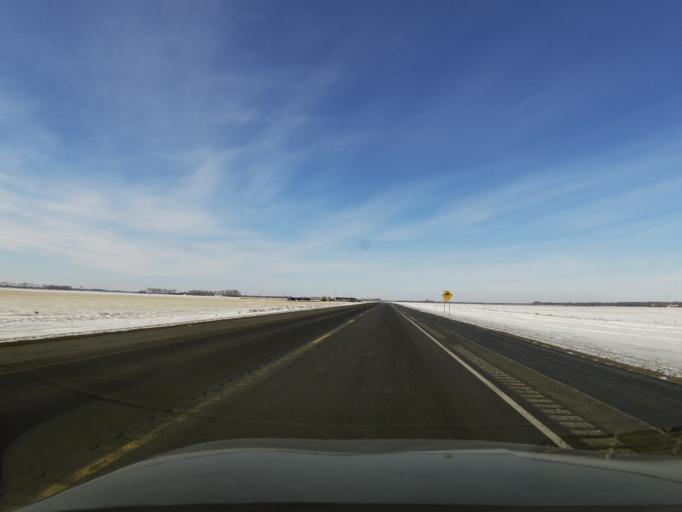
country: US
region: North Dakota
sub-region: Walsh County
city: Grafton
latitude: 48.4125
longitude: -97.4760
